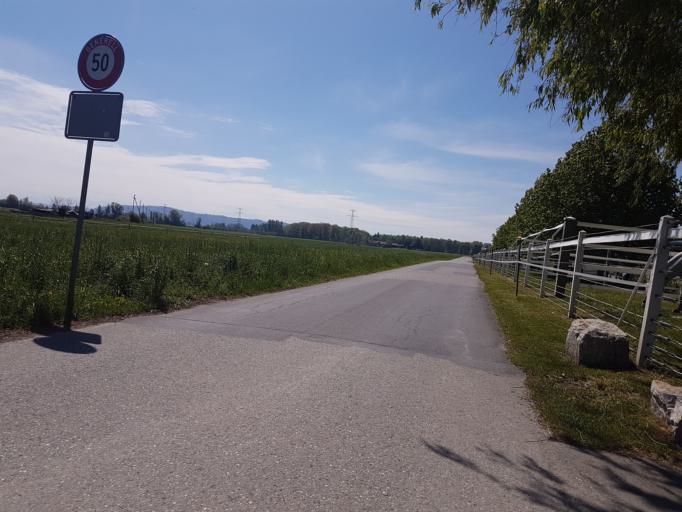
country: CH
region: Neuchatel
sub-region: Neuchatel District
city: Cornaux
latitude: 47.0200
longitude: 7.0364
